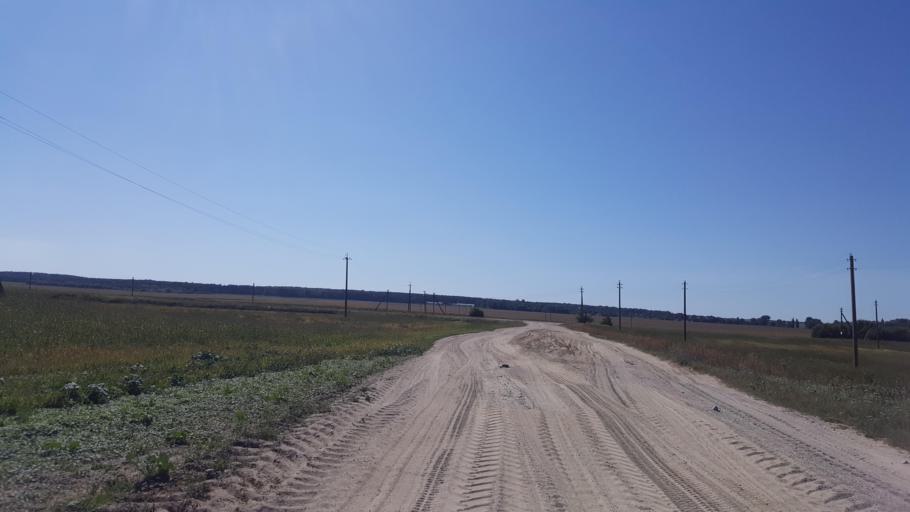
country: PL
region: Lublin Voivodeship
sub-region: Powiat bialski
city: Terespol
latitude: 52.2138
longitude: 23.5165
